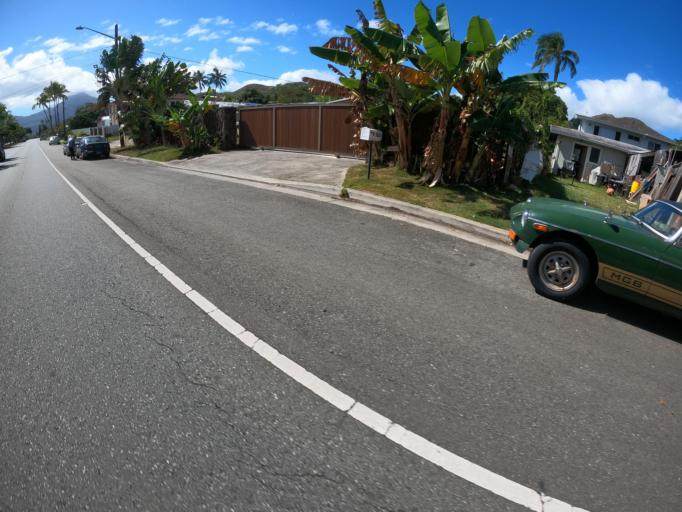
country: US
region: Hawaii
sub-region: Honolulu County
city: Kailua
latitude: 21.4182
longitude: -157.7499
